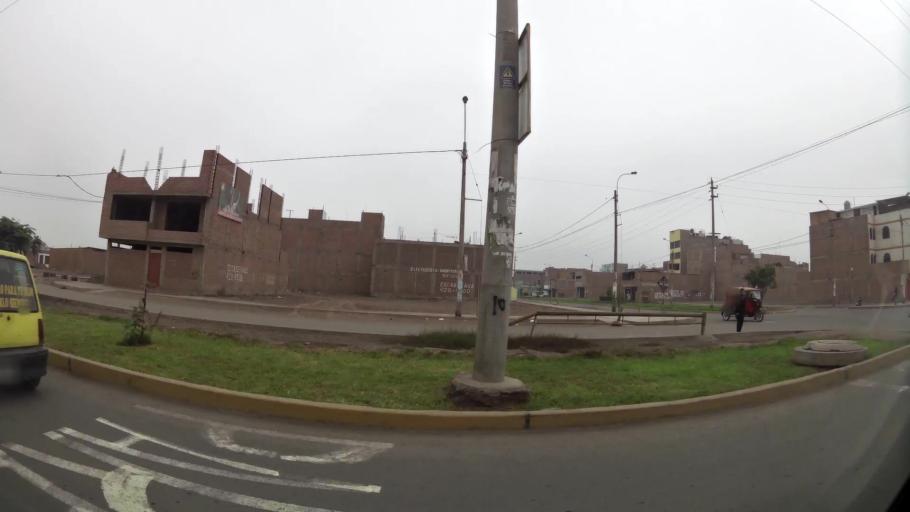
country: PE
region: Lima
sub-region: Lima
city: Urb. Santo Domingo
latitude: -11.8810
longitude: -77.0356
